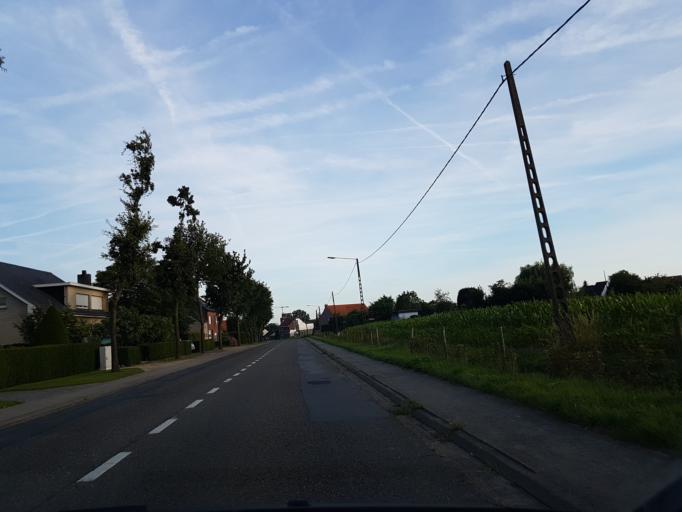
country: BE
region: Flanders
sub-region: Provincie Vlaams-Brabant
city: Merchtem
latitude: 50.9713
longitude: 4.2318
